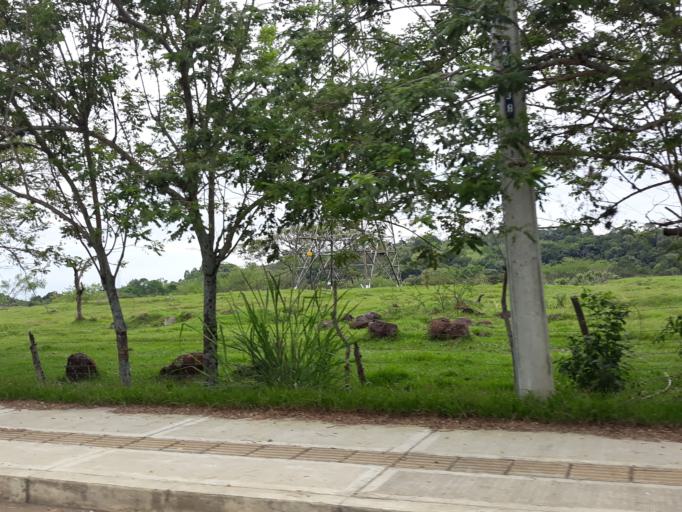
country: CO
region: Valle del Cauca
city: Jamundi
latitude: 3.3477
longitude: -76.5550
